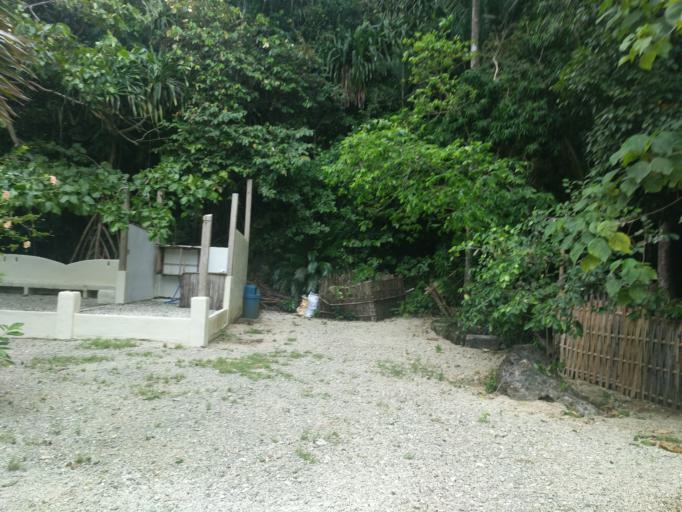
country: PH
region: Western Visayas
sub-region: Province of Negros Occidental
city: Bulata
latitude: 9.8765
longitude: 122.3781
